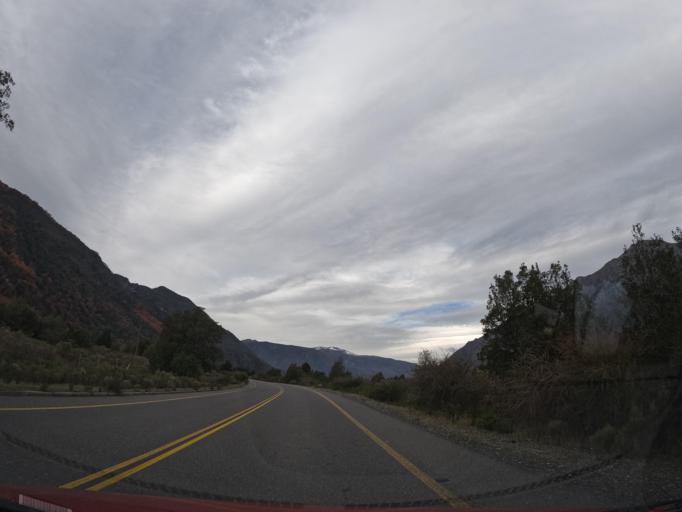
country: CL
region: Maule
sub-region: Provincia de Linares
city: Colbun
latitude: -35.7139
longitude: -71.0590
